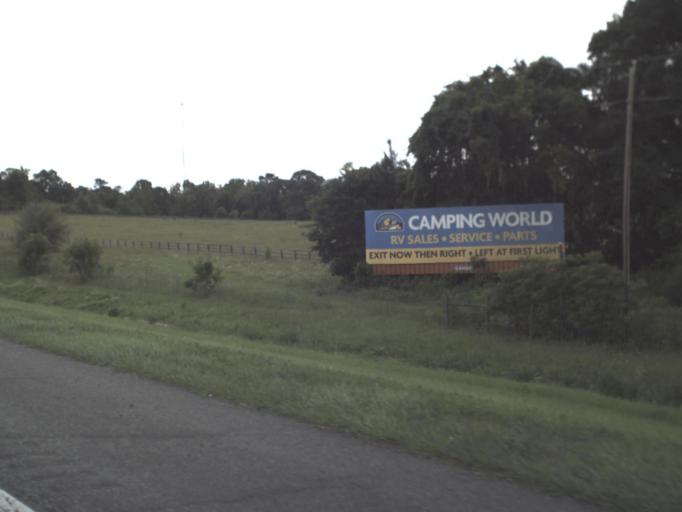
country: US
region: Florida
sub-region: Suwannee County
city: Wellborn
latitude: 30.2317
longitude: -82.7278
